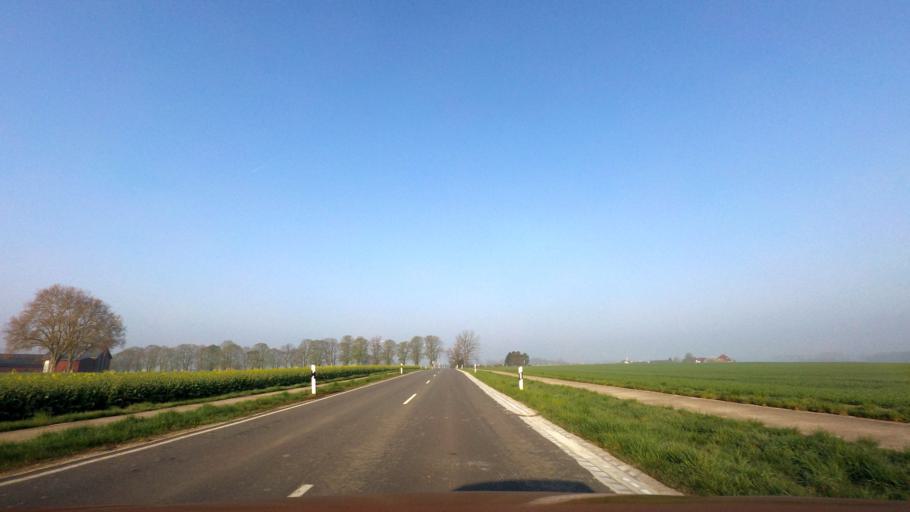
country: DE
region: Lower Saxony
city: Neuenkirchen
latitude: 52.1804
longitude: 8.4119
